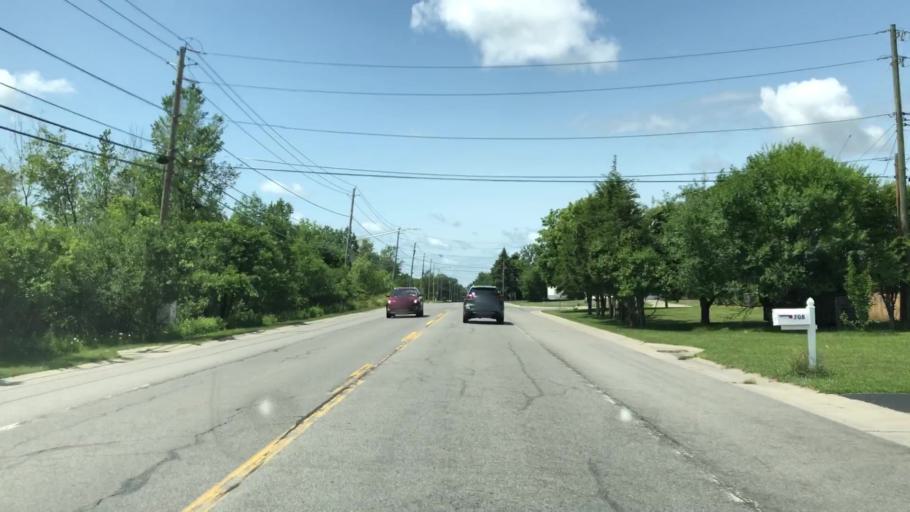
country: US
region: New York
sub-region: Erie County
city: Orchard Park
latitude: 42.8113
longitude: -78.7359
